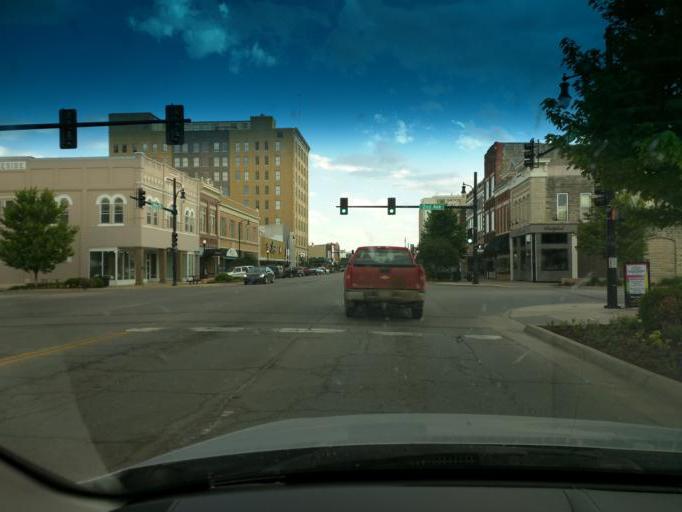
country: US
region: Kansas
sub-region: Reno County
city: Hutchinson
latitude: 38.0551
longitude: -97.9318
